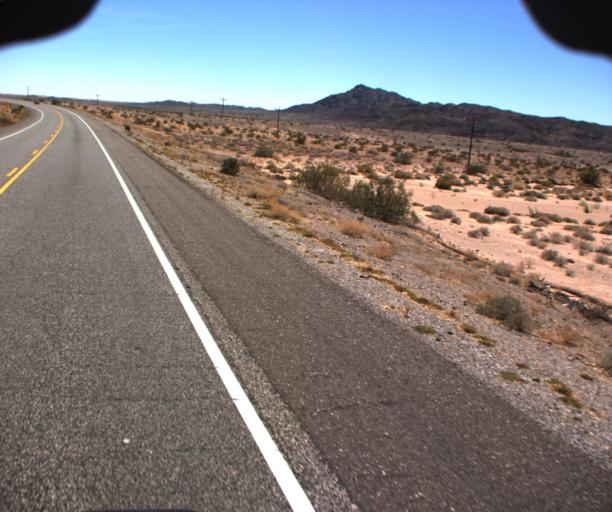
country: US
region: Arizona
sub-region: La Paz County
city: Parker
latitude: 34.0353
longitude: -114.2585
